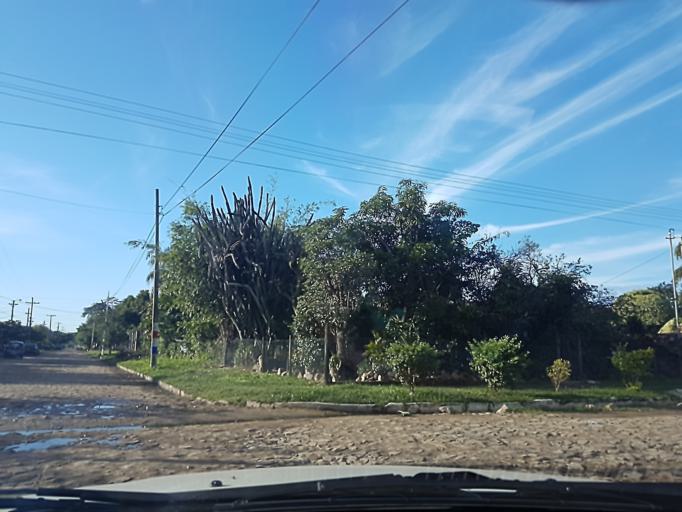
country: PY
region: Central
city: Colonia Mariano Roque Alonso
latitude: -25.2104
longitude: -57.5351
